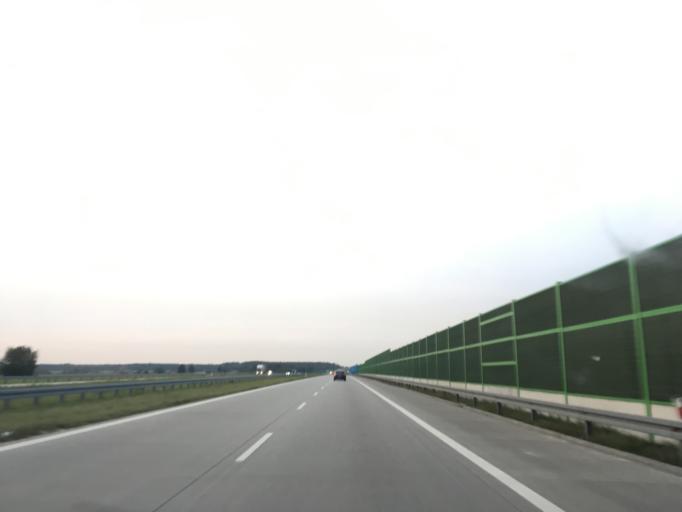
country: PL
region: Lodz Voivodeship
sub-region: Powiat lodzki wschodni
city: Tuszyn
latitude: 51.5782
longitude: 19.5943
